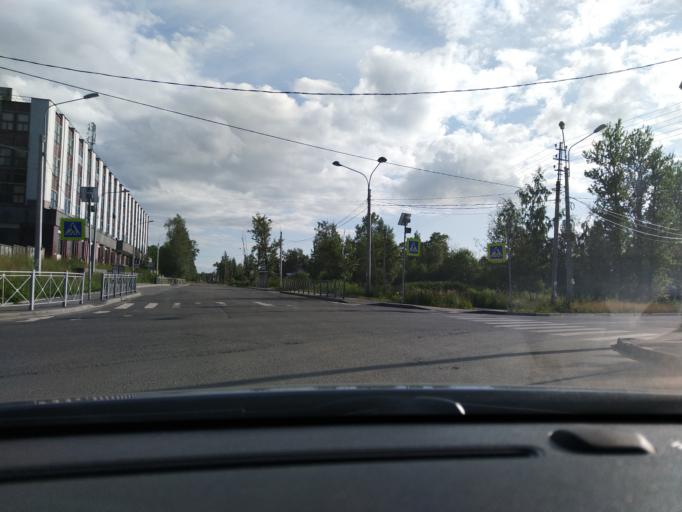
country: RU
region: St.-Petersburg
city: Gorelovo
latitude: 59.7807
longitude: 30.1498
